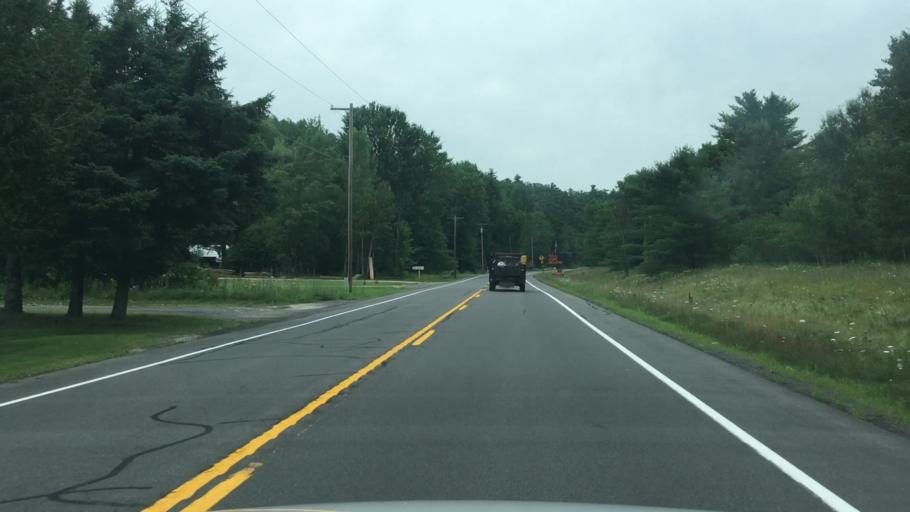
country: US
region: New York
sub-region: Clinton County
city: Peru
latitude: 44.4460
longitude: -73.6586
